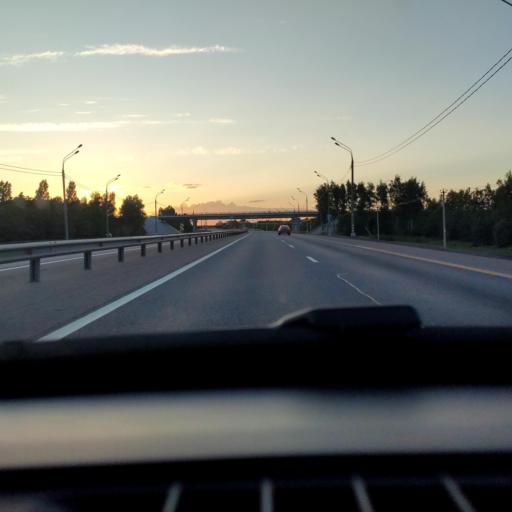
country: RU
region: Lipetsk
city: Khlevnoye
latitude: 52.2097
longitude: 39.1541
